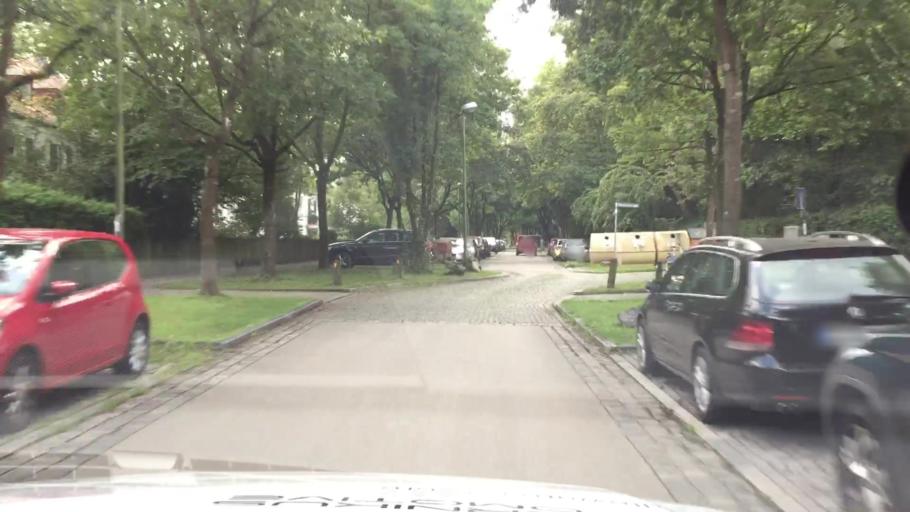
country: DE
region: Bavaria
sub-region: Upper Bavaria
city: Bogenhausen
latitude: 48.1715
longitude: 11.6046
